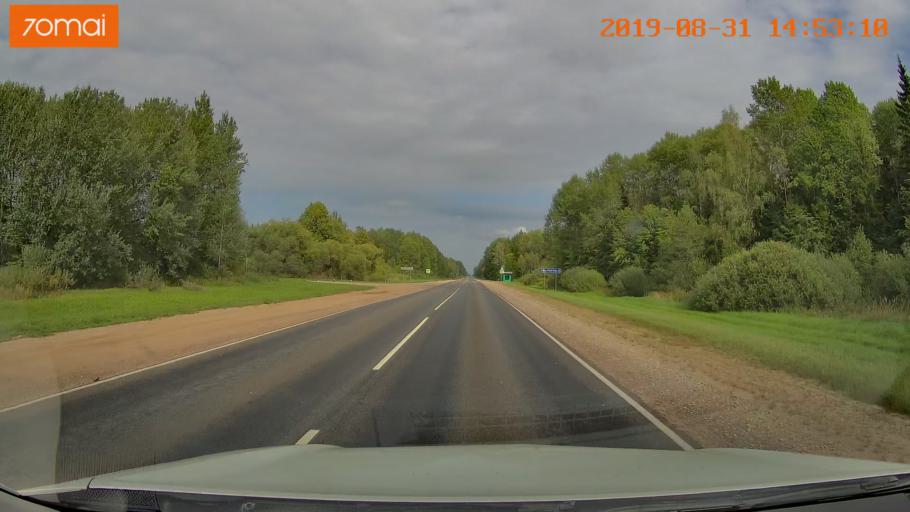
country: RU
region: Kaluga
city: Spas-Demensk
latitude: 54.2814
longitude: 33.8579
